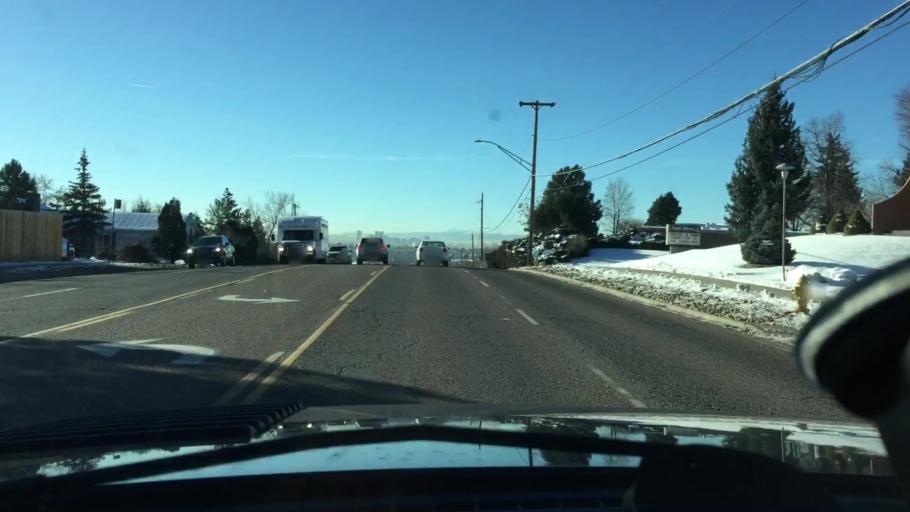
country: US
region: Colorado
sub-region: Adams County
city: Northglenn
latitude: 39.8762
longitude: -104.9967
